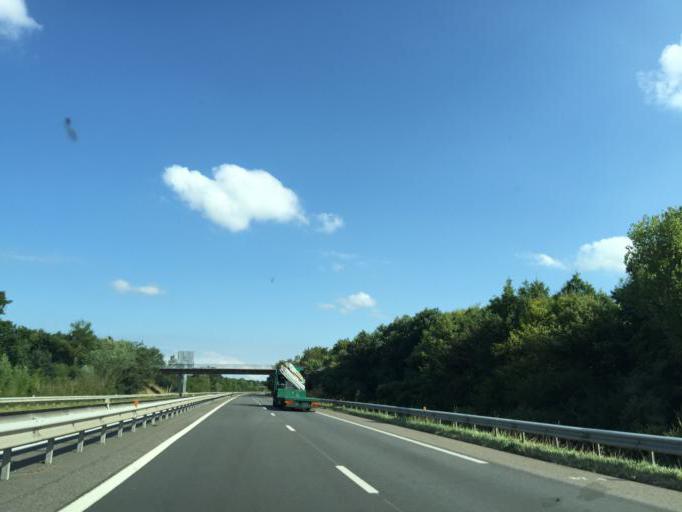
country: FR
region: Rhone-Alpes
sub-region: Departement de la Loire
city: Balbigny
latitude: 45.7999
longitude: 4.1283
